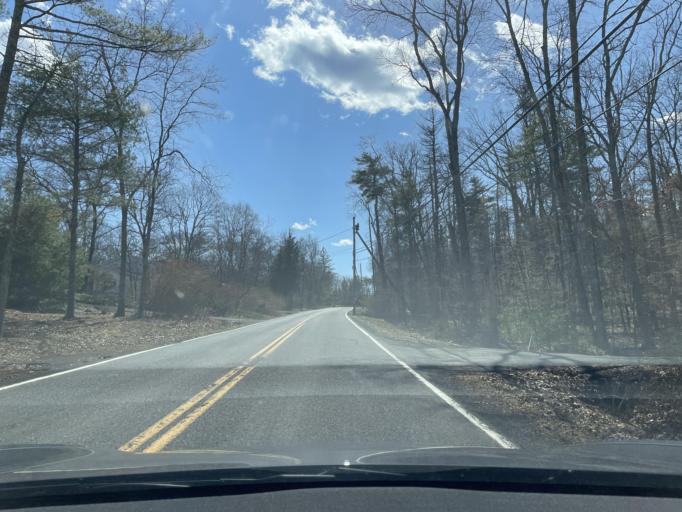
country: US
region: New York
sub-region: Ulster County
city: West Hurley
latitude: 41.9672
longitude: -74.0991
